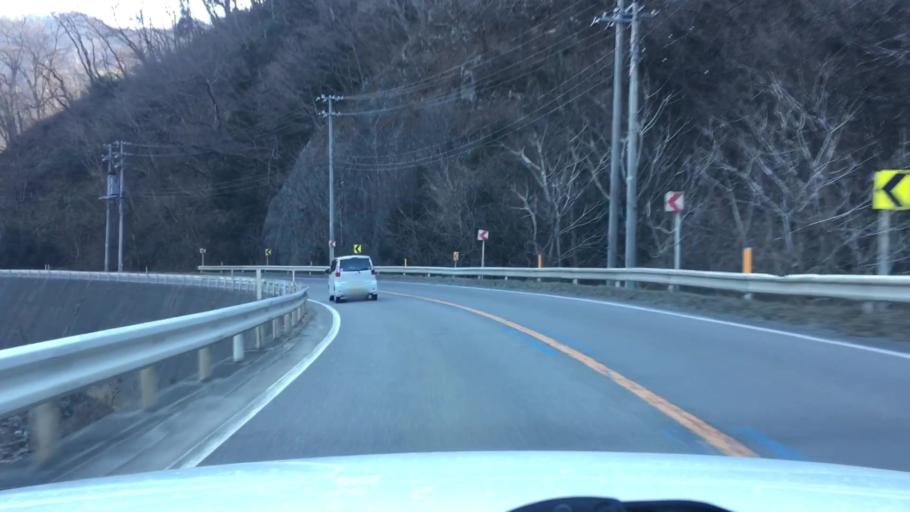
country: JP
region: Iwate
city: Miyako
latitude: 39.6063
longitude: 141.7720
